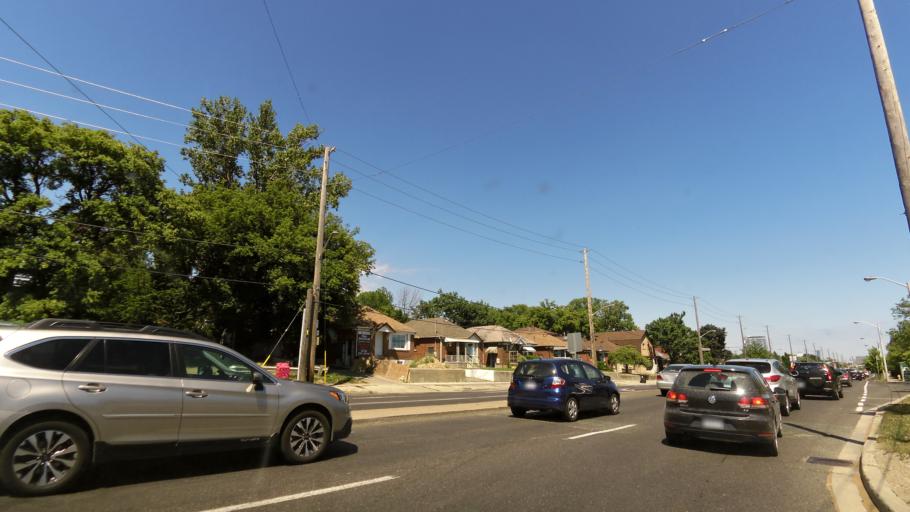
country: CA
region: Ontario
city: Etobicoke
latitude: 43.6290
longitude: -79.4900
